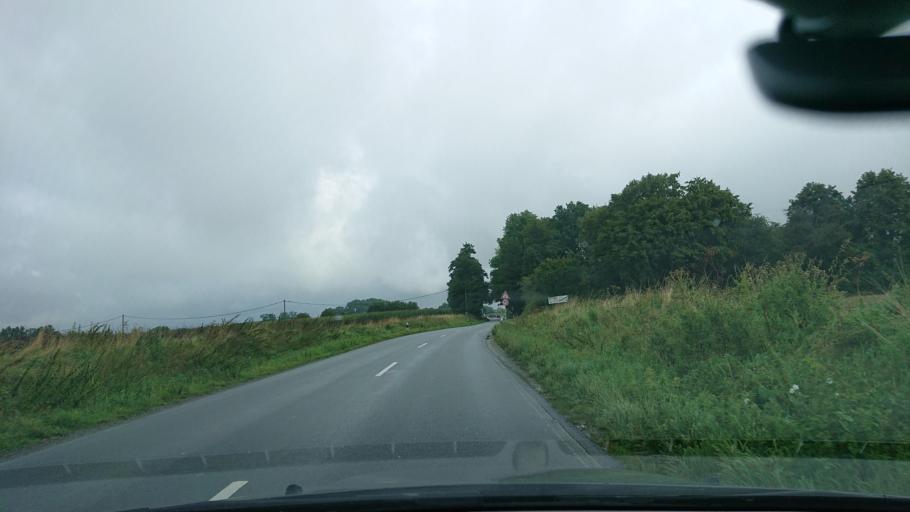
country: DE
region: North Rhine-Westphalia
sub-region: Regierungsbezirk Arnsberg
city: Soest
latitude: 51.5911
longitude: 8.1253
